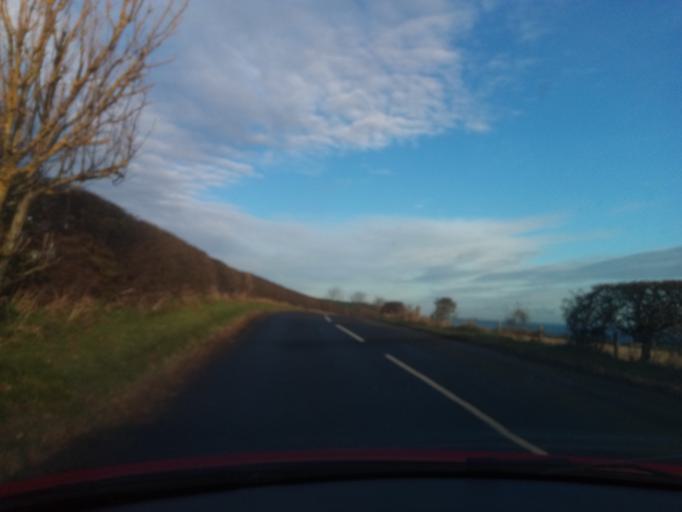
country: GB
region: Scotland
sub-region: The Scottish Borders
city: Eyemouth
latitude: 55.8948
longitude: -2.1439
